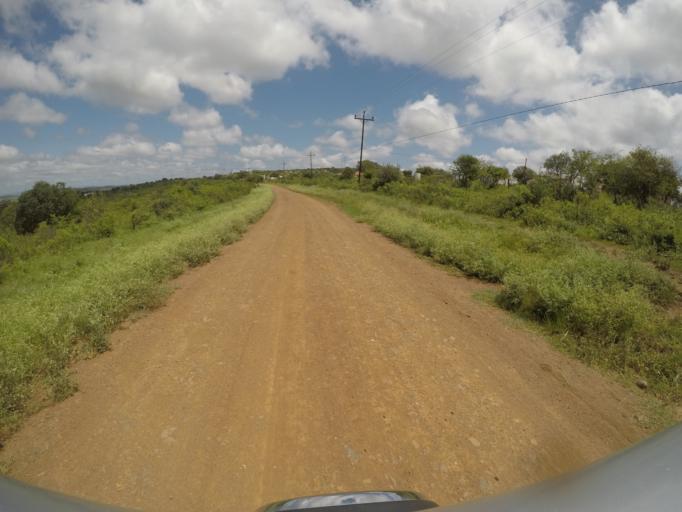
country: ZA
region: KwaZulu-Natal
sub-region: uThungulu District Municipality
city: Empangeni
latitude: -28.5861
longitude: 31.8233
